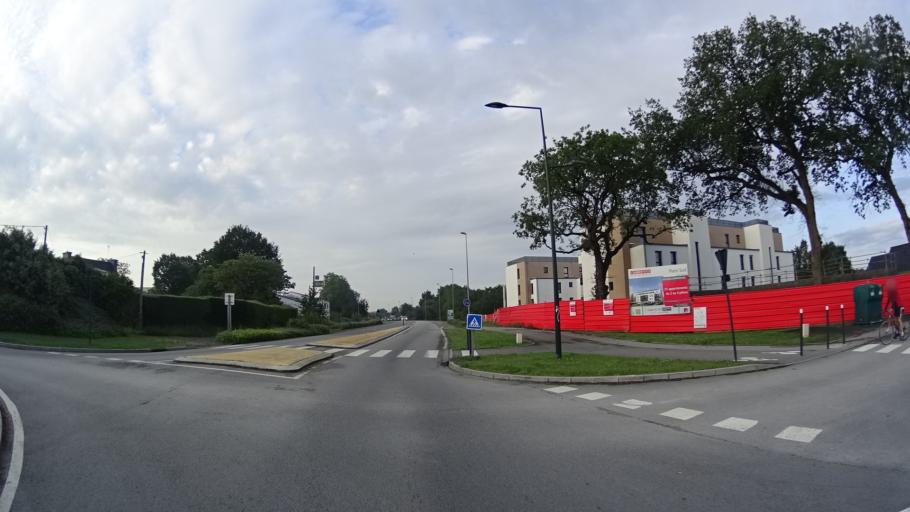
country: FR
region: Brittany
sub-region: Departement du Morbihan
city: Vannes
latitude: 47.6491
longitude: -2.7233
